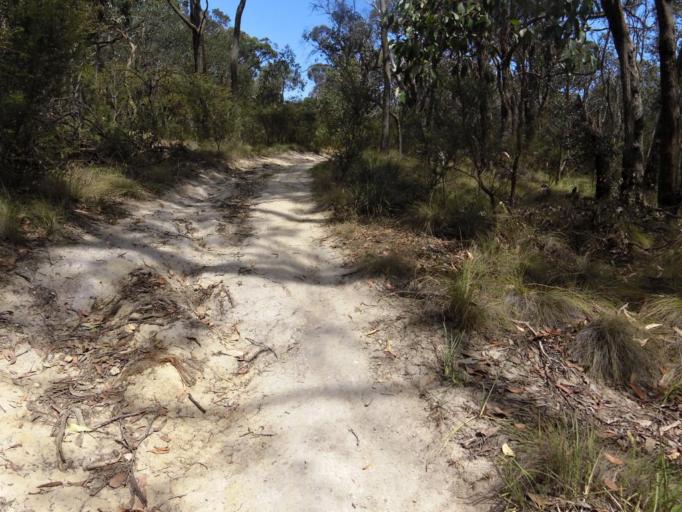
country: AU
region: Victoria
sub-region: Melton
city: Melton West
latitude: -37.5042
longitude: 144.5480
